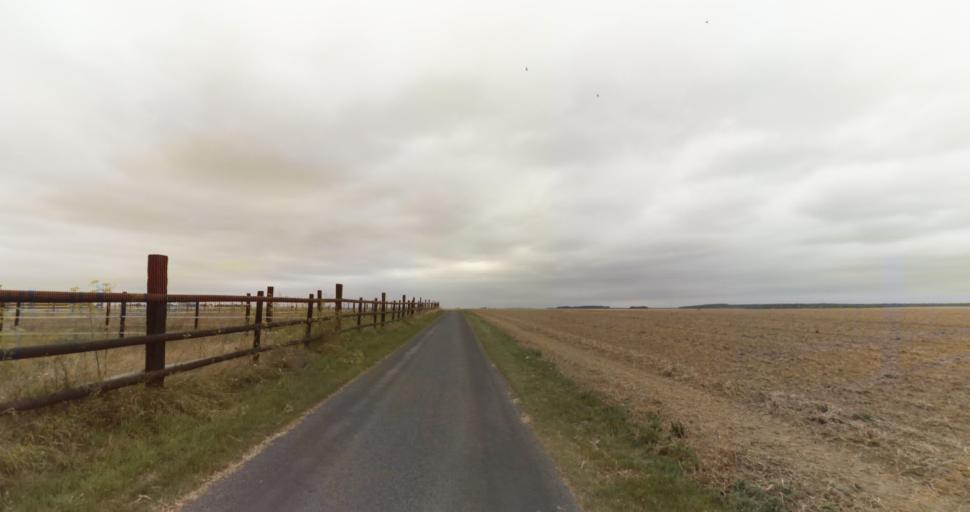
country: FR
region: Haute-Normandie
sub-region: Departement de l'Eure
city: La Couture-Boussey
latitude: 48.9313
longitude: 1.3282
